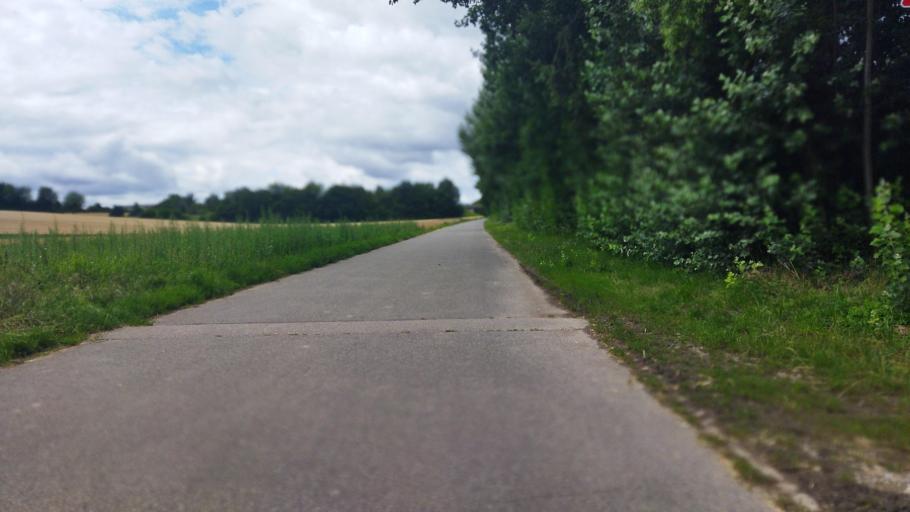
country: DE
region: Baden-Wuerttemberg
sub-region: Regierungsbezirk Stuttgart
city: Bad Rappenau
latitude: 49.2139
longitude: 9.0864
